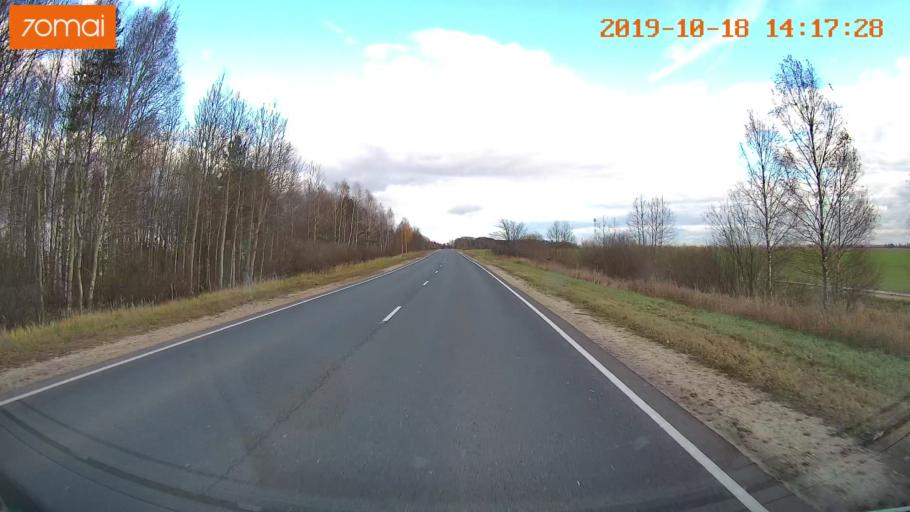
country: RU
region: Rjazan
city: Tuma
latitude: 55.1390
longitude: 40.3732
